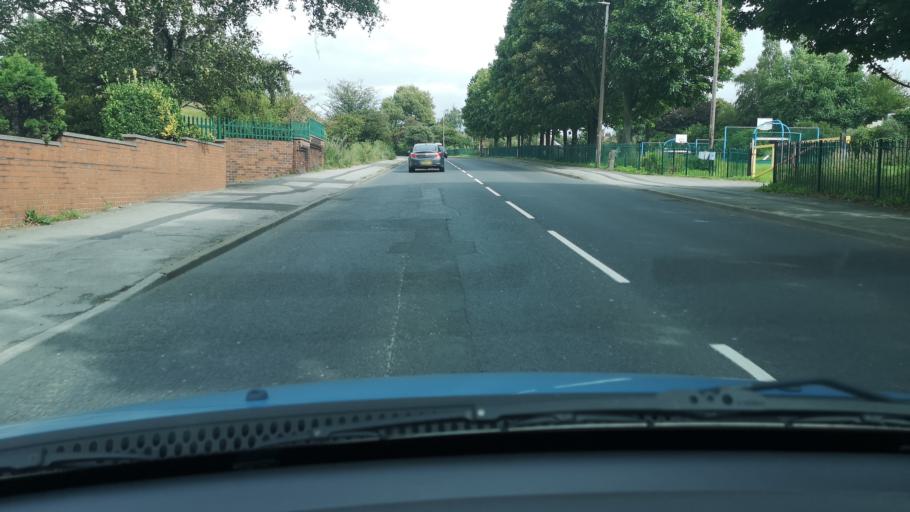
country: GB
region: England
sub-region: Barnsley
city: Cudworth
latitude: 53.5731
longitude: -1.4254
